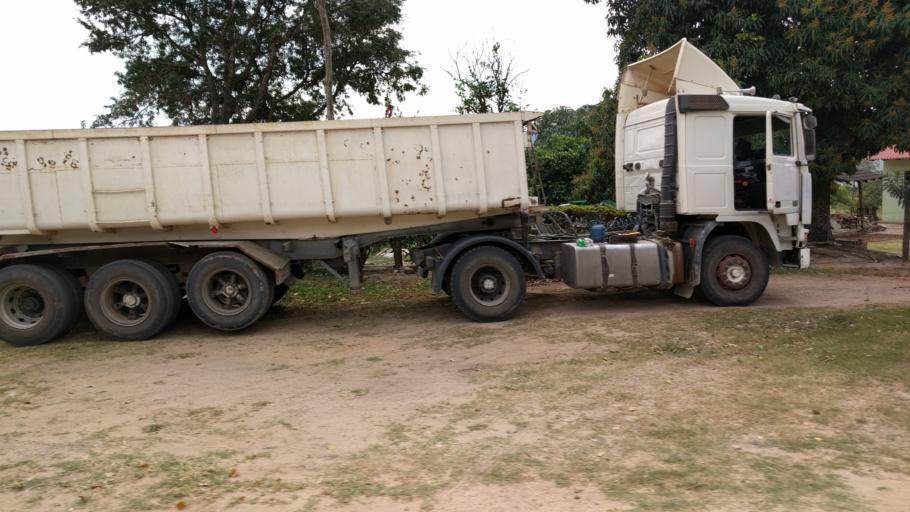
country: BO
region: Santa Cruz
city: Limoncito
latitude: -18.0414
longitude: -63.4134
